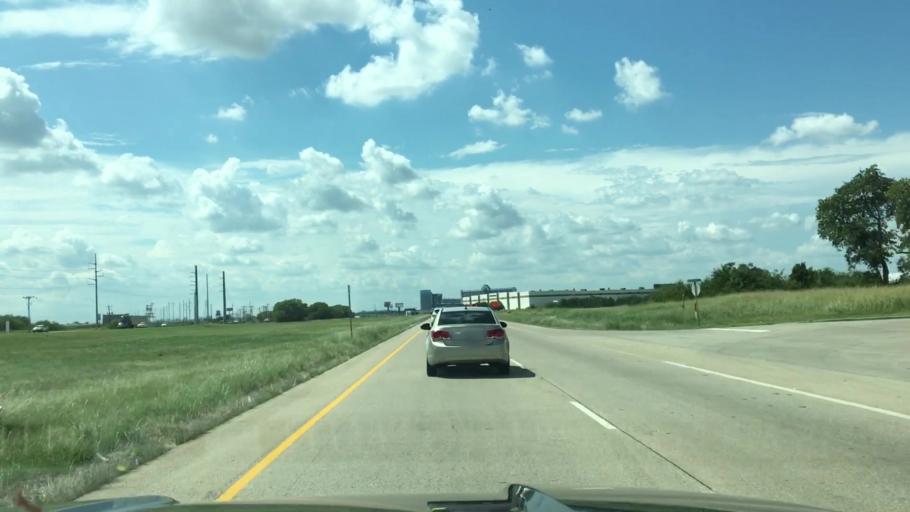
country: US
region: Texas
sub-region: Denton County
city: Roanoke
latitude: 33.0252
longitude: -97.2606
